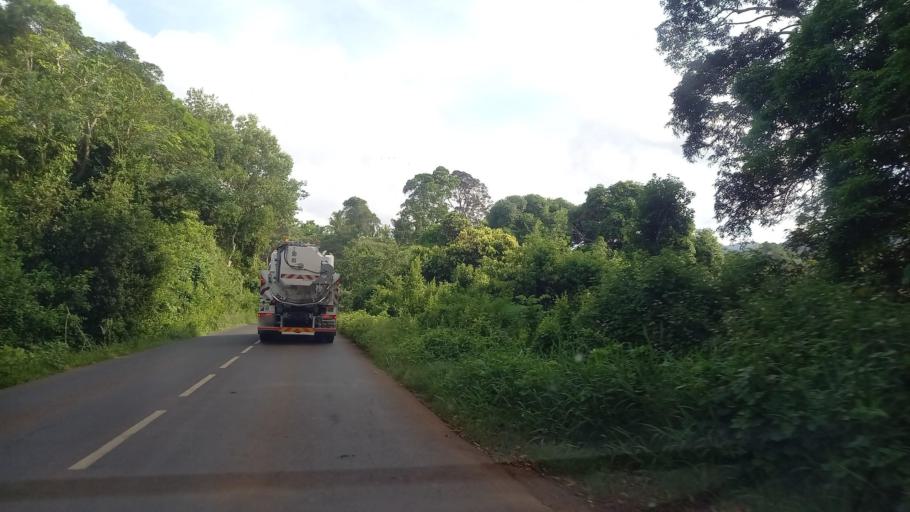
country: YT
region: Chiconi
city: Chiconi
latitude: -12.8195
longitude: 45.1288
